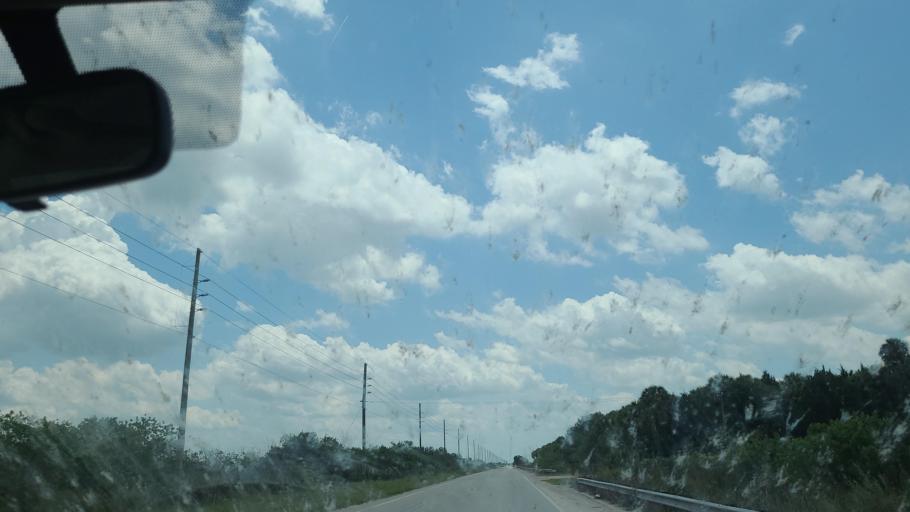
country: US
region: Florida
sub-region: Glades County
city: Buckhead Ridge
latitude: 27.1990
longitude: -81.0944
